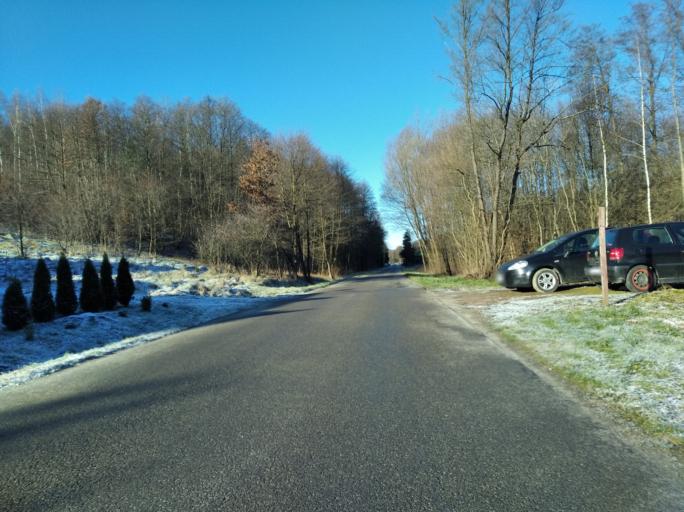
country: PL
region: Subcarpathian Voivodeship
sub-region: Powiat strzyzowski
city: Czudec
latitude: 49.9468
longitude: 21.7846
